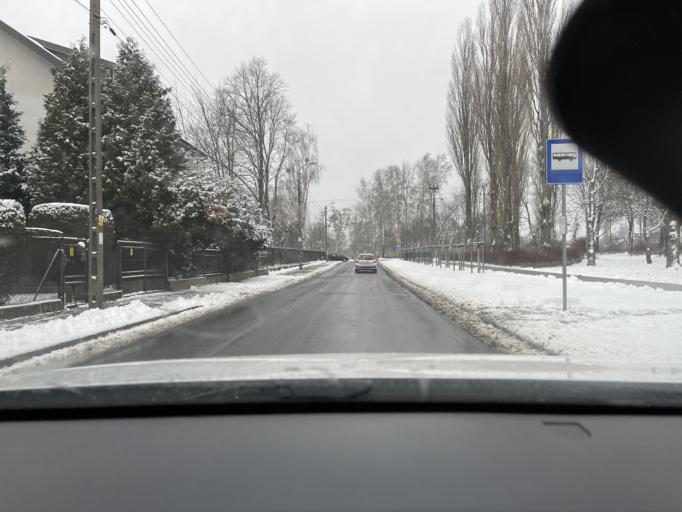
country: PL
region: Masovian Voivodeship
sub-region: Powiat zyrardowski
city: Zyrardow
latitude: 52.0463
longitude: 20.4423
